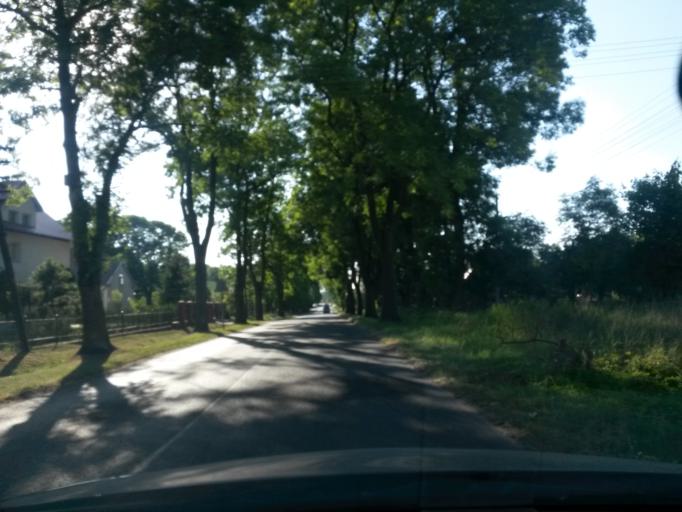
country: PL
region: Kujawsko-Pomorskie
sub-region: Powiat rypinski
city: Skrwilno
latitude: 53.0576
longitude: 19.6118
